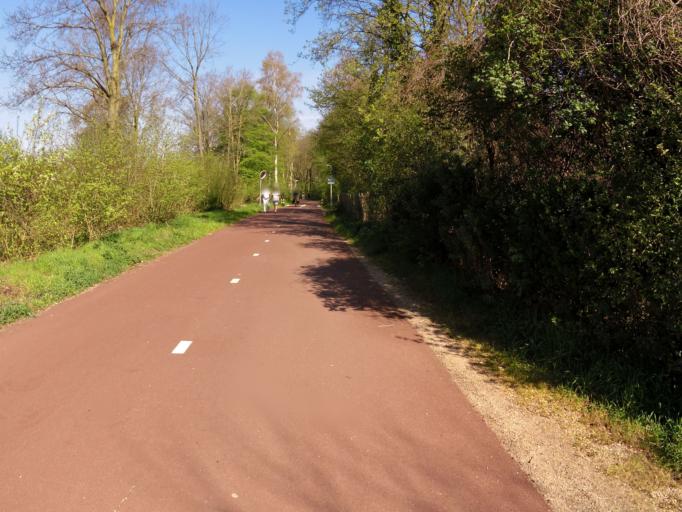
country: NL
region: North Brabant
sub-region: Gemeente Cuijk
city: Cuijk
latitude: 51.7767
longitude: 5.8671
